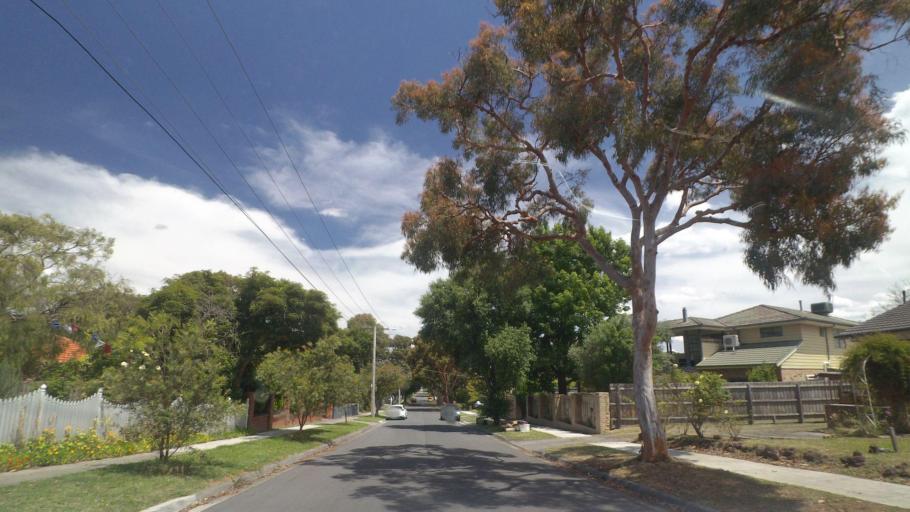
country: AU
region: Victoria
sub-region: Knox
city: Boronia
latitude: -37.8479
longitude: 145.2945
